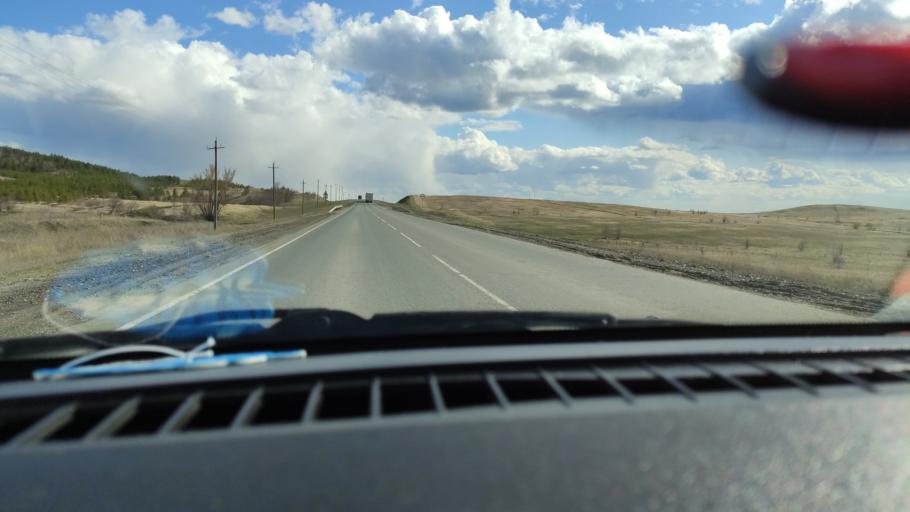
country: RU
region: Saratov
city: Alekseyevka
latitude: 52.3018
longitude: 47.9269
